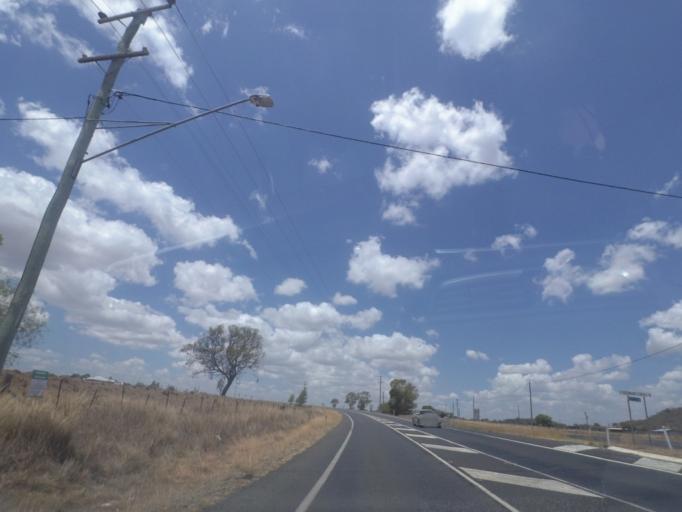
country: AU
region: Queensland
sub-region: Toowoomba
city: Top Camp
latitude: -27.7315
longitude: 151.9122
